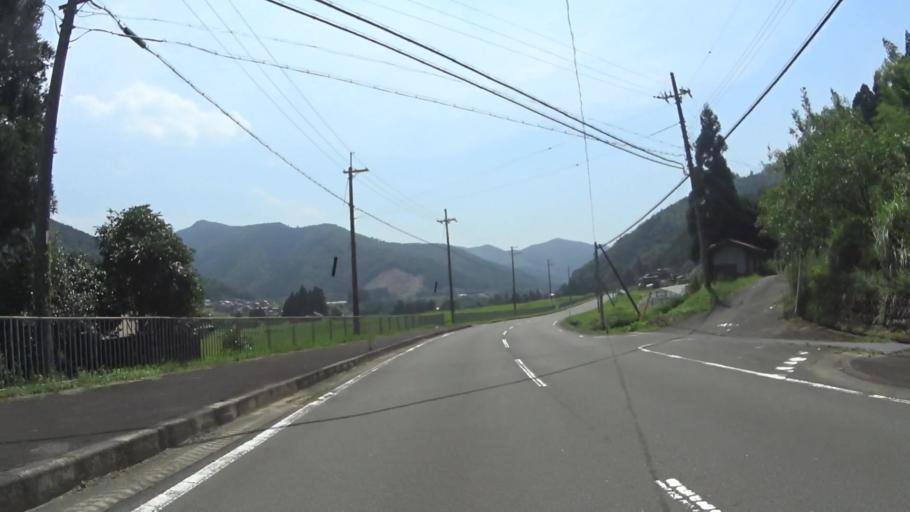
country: JP
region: Kyoto
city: Ayabe
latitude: 35.2737
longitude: 135.4321
